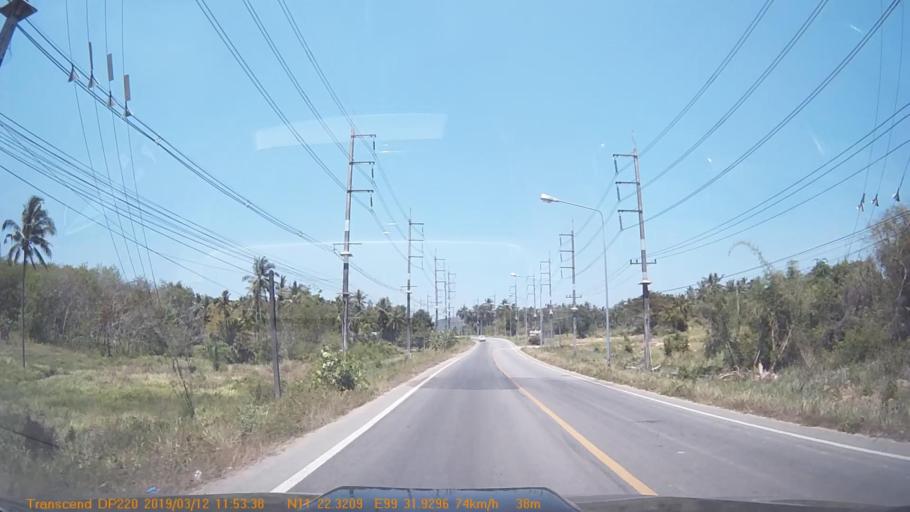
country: TH
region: Prachuap Khiri Khan
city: Thap Sakae
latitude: 11.3721
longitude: 99.5321
